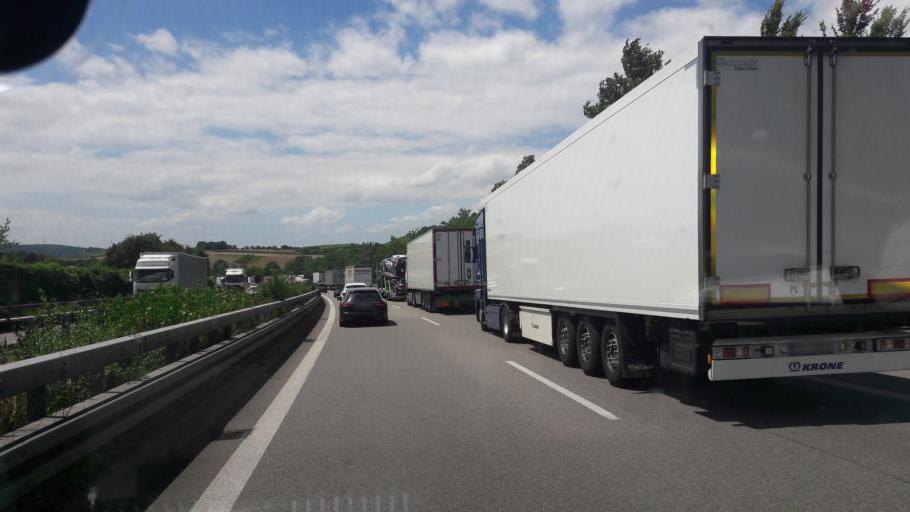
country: DE
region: Baden-Wuerttemberg
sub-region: Regierungsbezirk Stuttgart
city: Ellhofen
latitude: 49.1627
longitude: 9.3323
